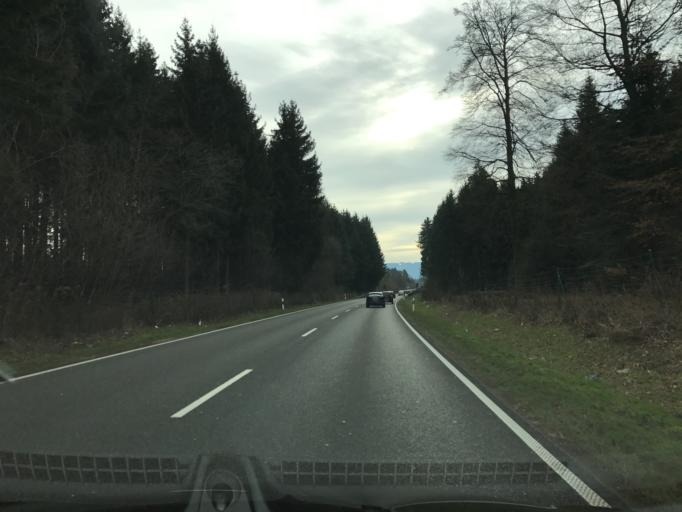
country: DE
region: Bavaria
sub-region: Swabia
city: Nonnenhorn
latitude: 47.5940
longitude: 9.6395
